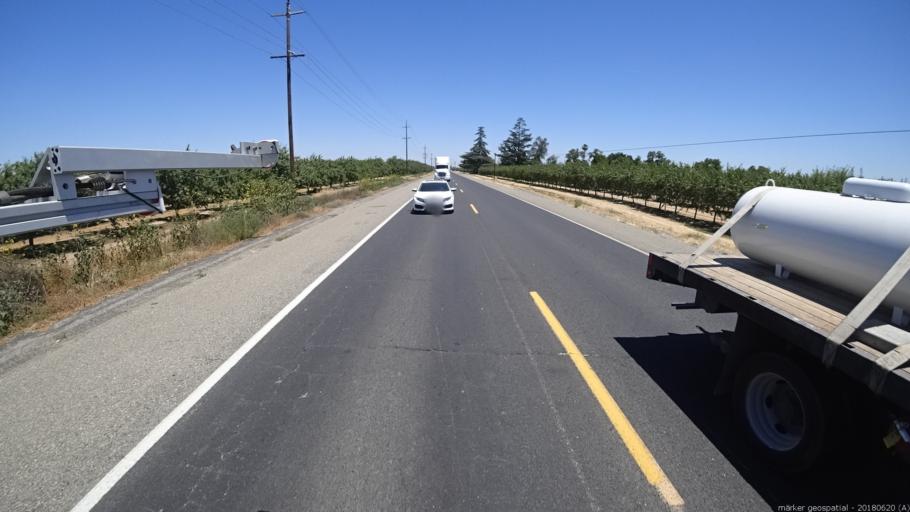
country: US
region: California
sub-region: Madera County
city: Parkwood
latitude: 36.9239
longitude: -120.0708
